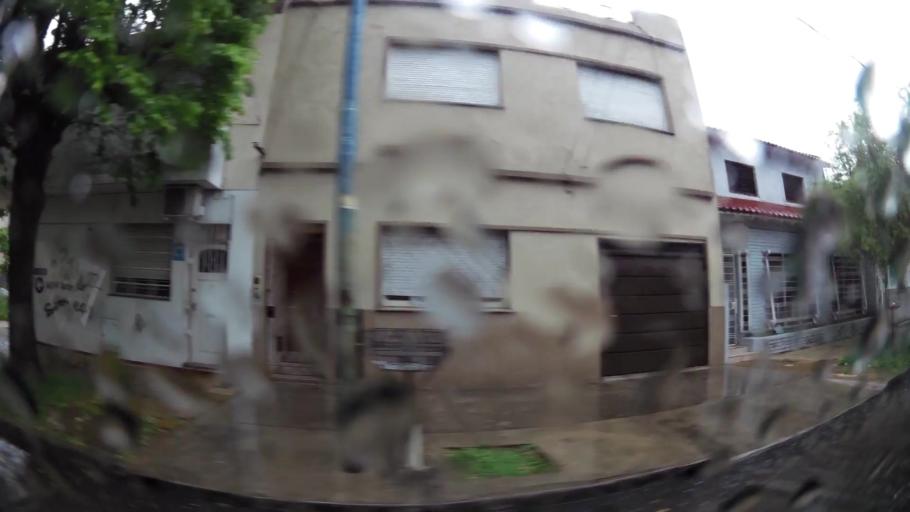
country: AR
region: Buenos Aires
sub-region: Partido de Lanus
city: Lanus
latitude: -34.7096
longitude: -58.3987
